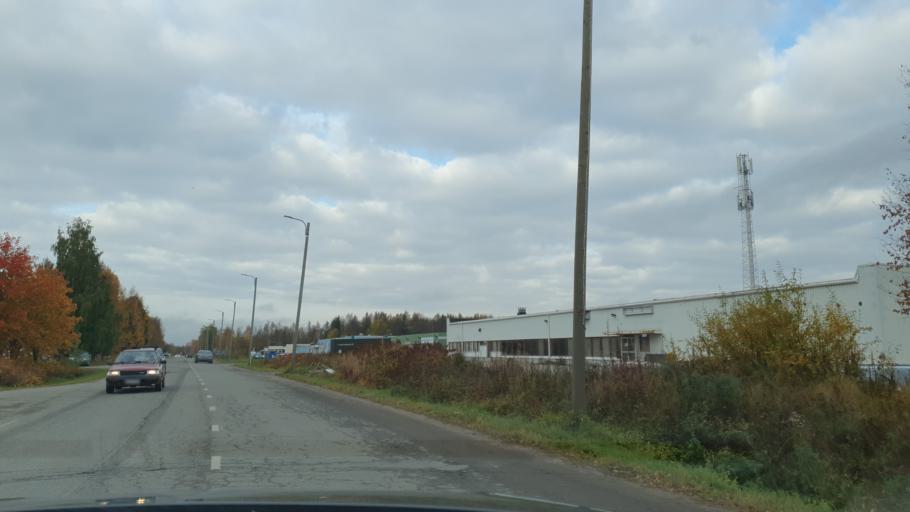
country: FI
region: Lapland
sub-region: Rovaniemi
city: Rovaniemi
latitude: 66.4916
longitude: 25.6720
